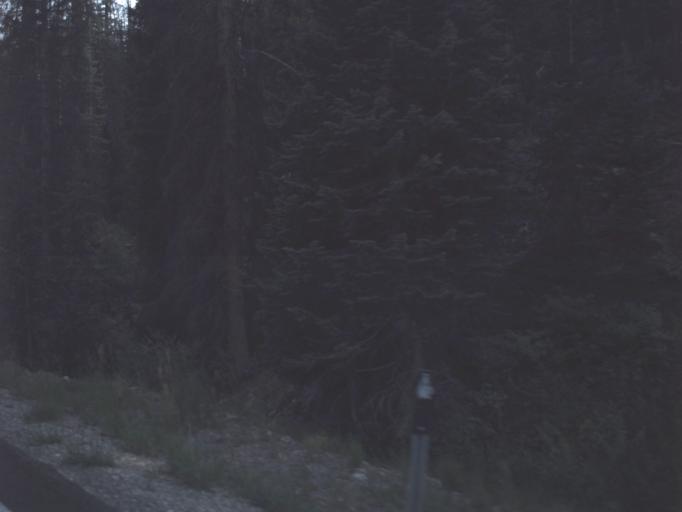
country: US
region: Utah
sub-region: Summit County
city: Kamas
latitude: 40.7691
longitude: -110.8832
